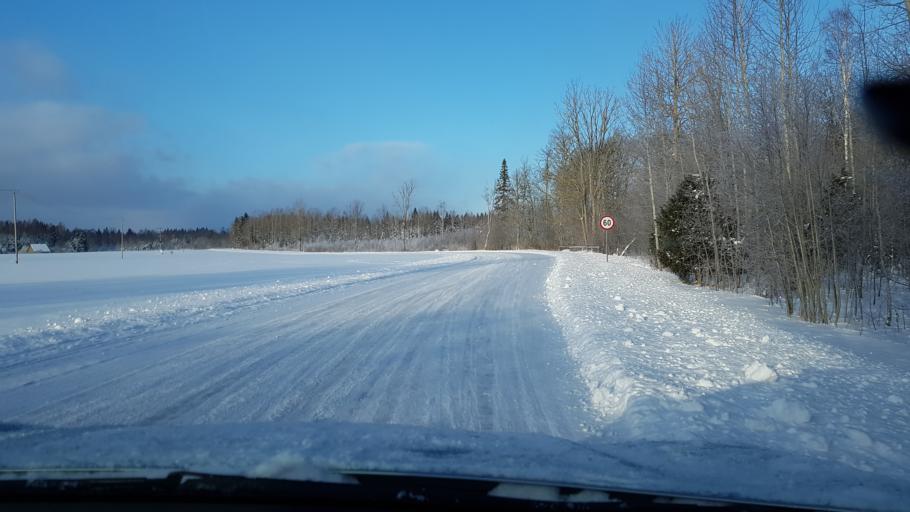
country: EE
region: Harju
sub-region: Nissi vald
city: Turba
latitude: 59.1084
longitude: 24.2287
